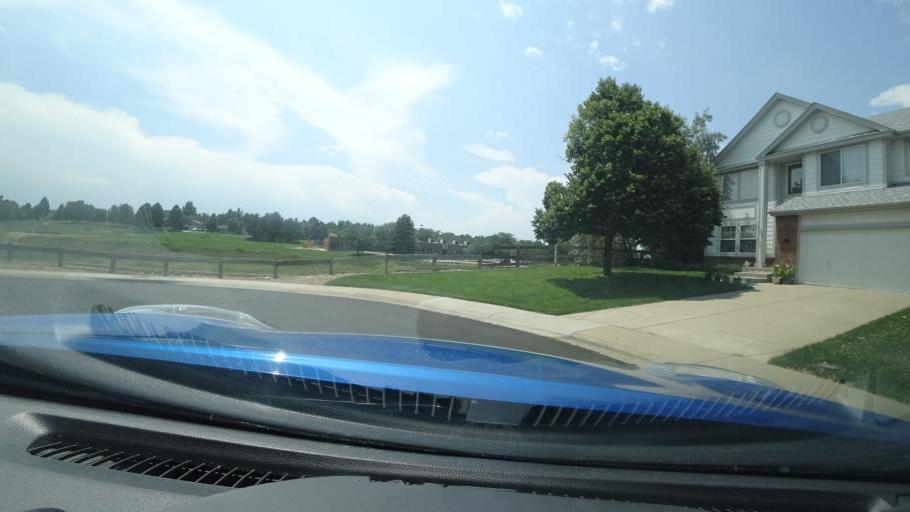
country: US
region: Colorado
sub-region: Adams County
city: Aurora
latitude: 39.6649
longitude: -104.7641
